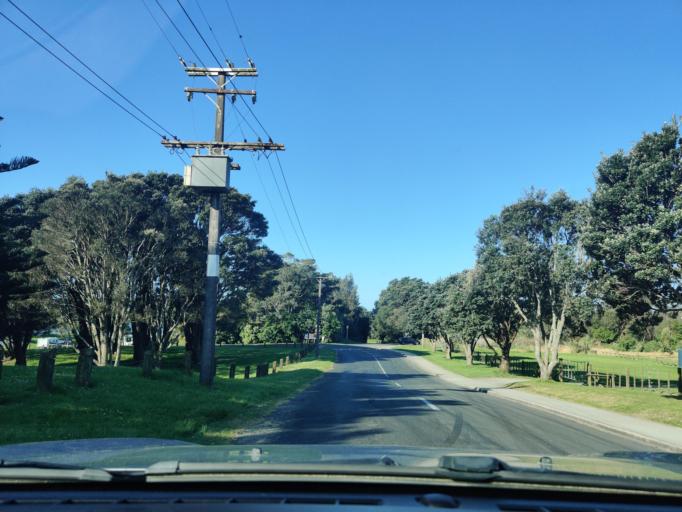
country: NZ
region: Taranaki
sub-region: New Plymouth District
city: New Plymouth
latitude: -39.0436
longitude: 174.1135
